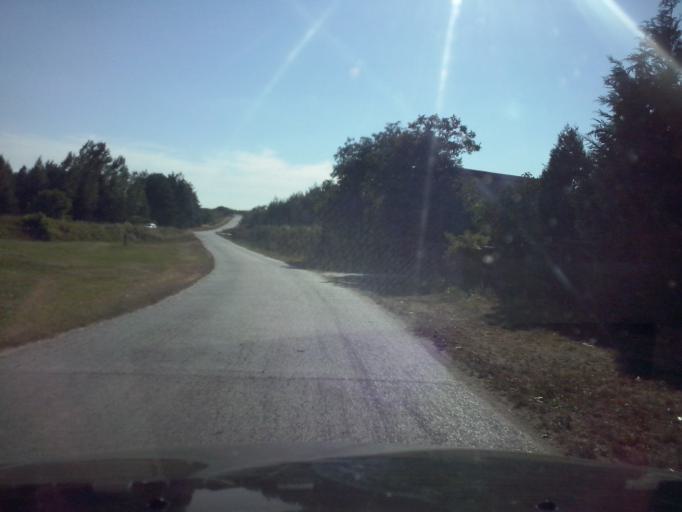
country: PL
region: Swietokrzyskie
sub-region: Powiat pinczowski
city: Kije
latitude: 50.5601
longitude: 20.6627
